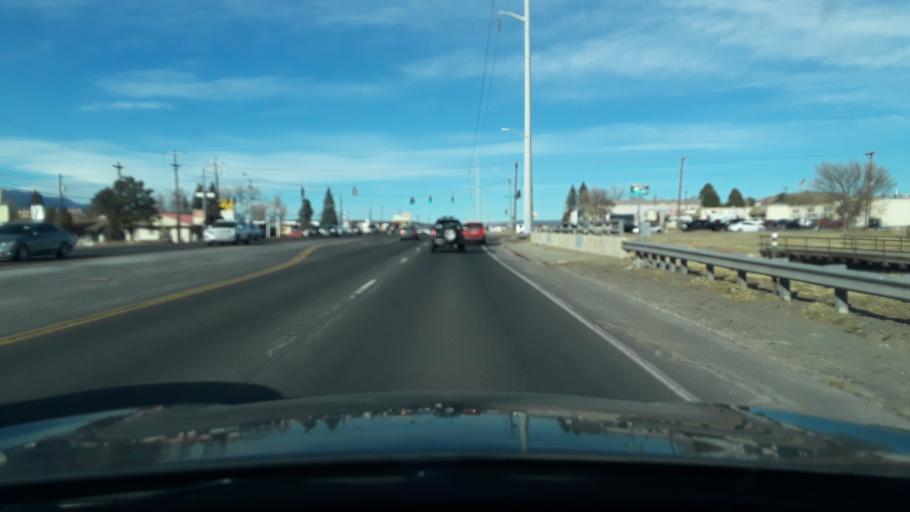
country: US
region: Colorado
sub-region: El Paso County
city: Colorado Springs
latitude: 38.8885
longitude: -104.8185
